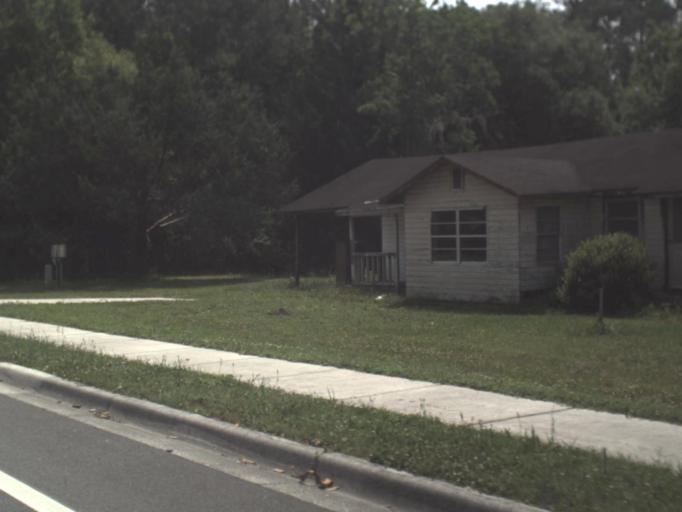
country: US
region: Florida
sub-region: Nassau County
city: Callahan
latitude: 30.5812
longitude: -81.8119
